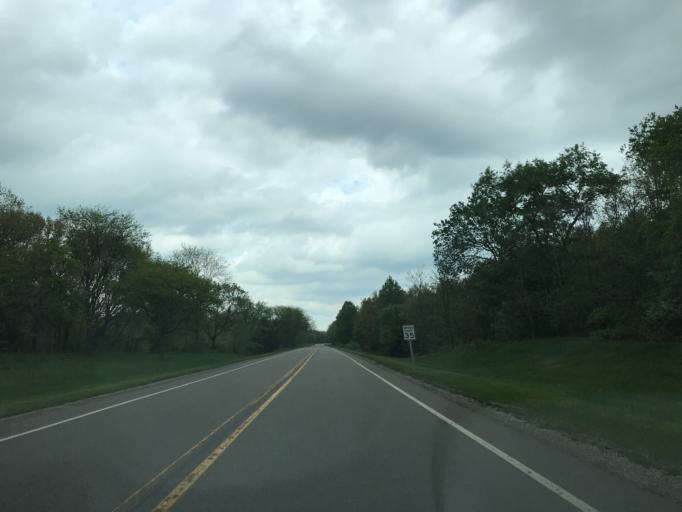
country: US
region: Michigan
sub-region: Oakland County
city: South Lyon
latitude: 42.5282
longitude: -83.6348
